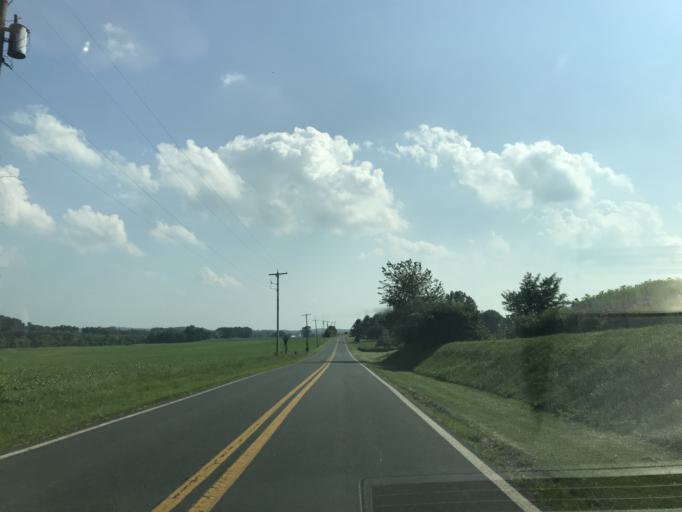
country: US
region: Maryland
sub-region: Carroll County
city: Westminster
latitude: 39.6258
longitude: -76.9717
